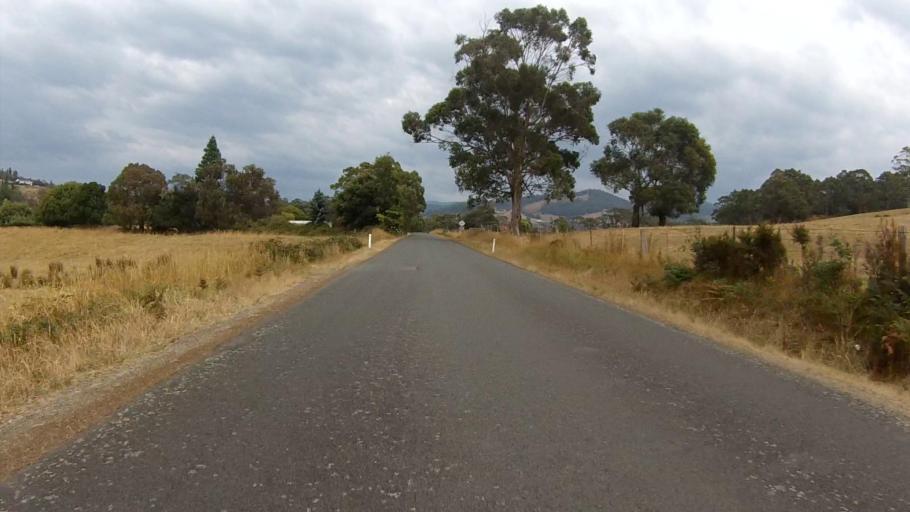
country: AU
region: Tasmania
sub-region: Huon Valley
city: Cygnet
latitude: -43.1833
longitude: 147.1104
